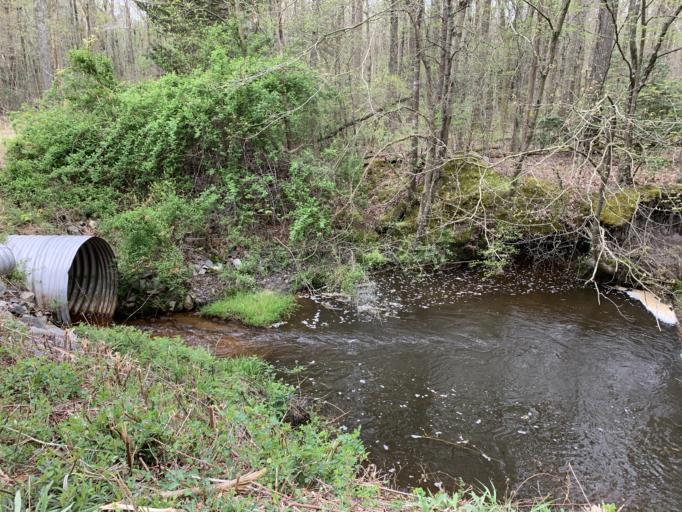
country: US
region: Delaware
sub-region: Kent County
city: Felton
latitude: 39.0268
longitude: -75.6338
